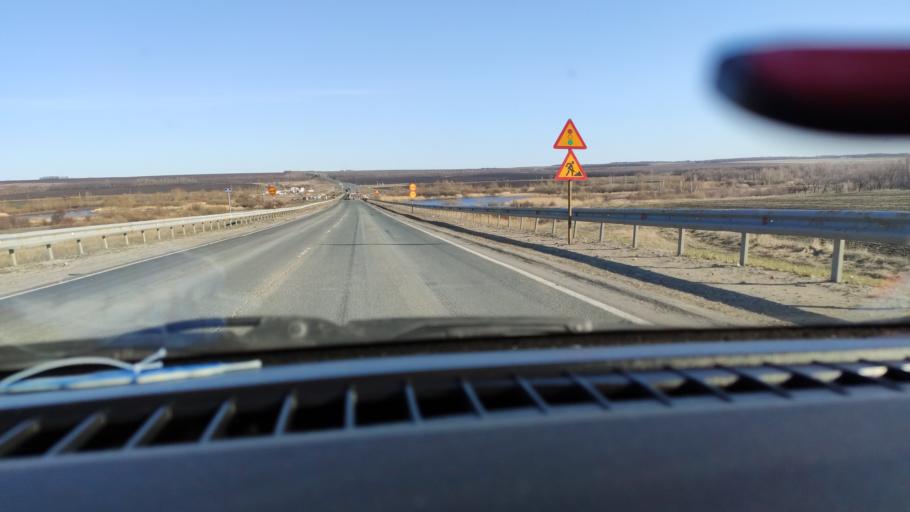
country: RU
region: Saratov
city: Dukhovnitskoye
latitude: 52.7343
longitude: 48.2570
